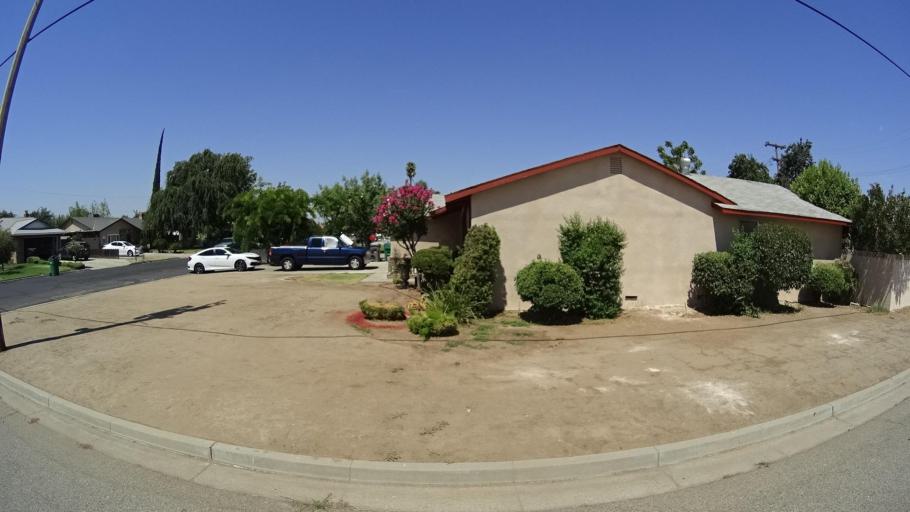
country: US
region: California
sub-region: Fresno County
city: Sunnyside
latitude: 36.7540
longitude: -119.7092
